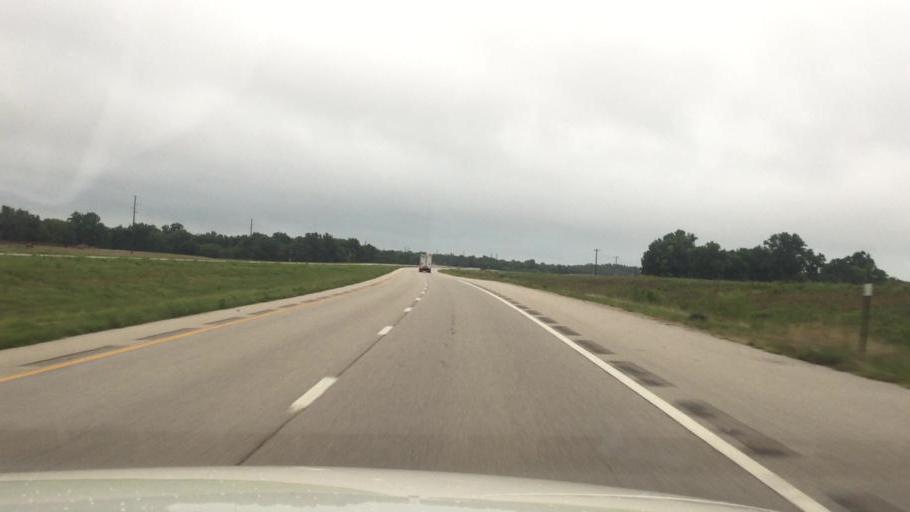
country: US
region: Kansas
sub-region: Montgomery County
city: Coffeyville
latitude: 37.0726
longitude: -95.5875
